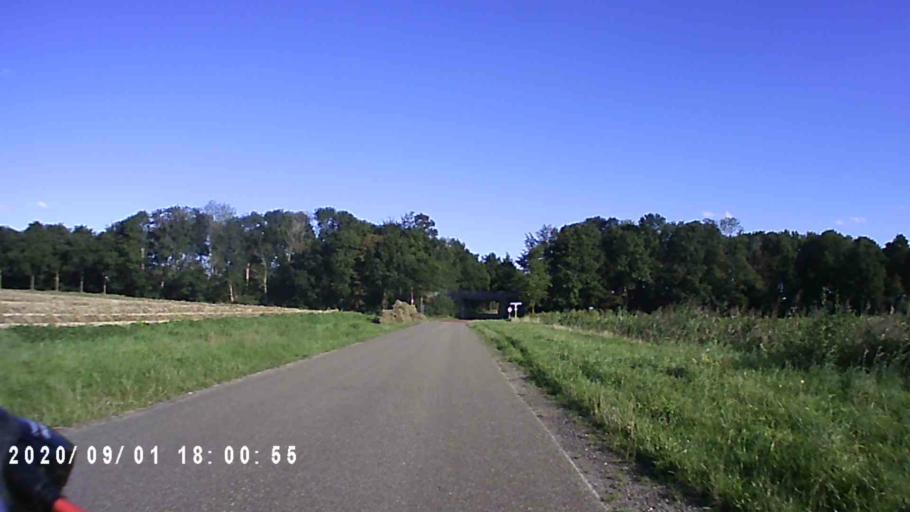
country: NL
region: Groningen
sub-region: Gemeente Slochteren
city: Slochteren
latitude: 53.2015
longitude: 6.7802
